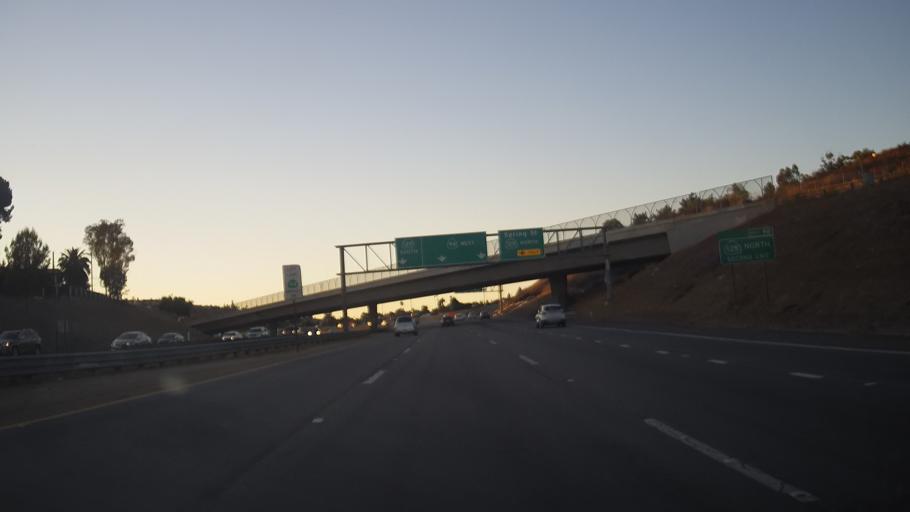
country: US
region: California
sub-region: San Diego County
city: Spring Valley
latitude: 32.7519
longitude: -117.0047
